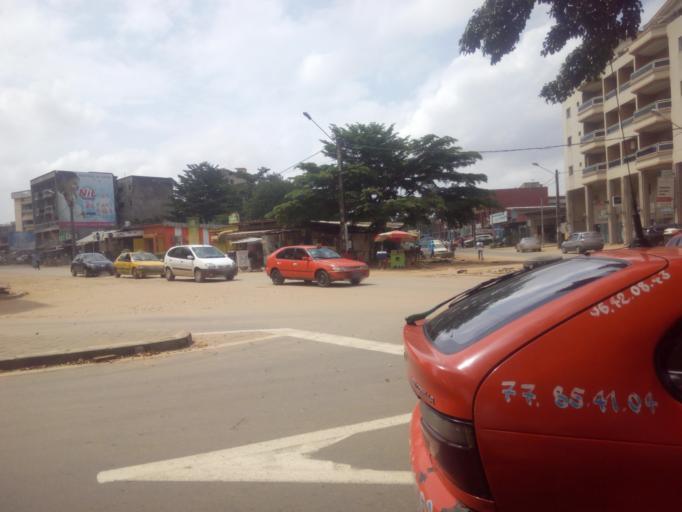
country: CI
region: Lagunes
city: Abidjan
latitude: 5.3639
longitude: -3.9619
